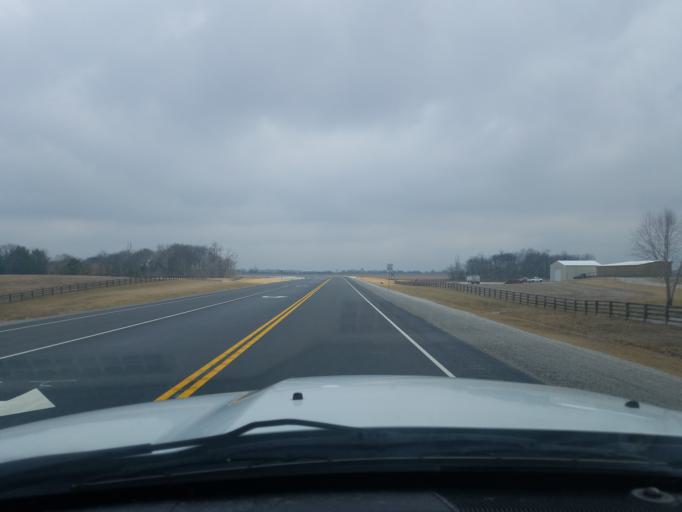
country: US
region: Kentucky
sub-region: Logan County
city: Russellville
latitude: 36.8062
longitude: -86.8893
